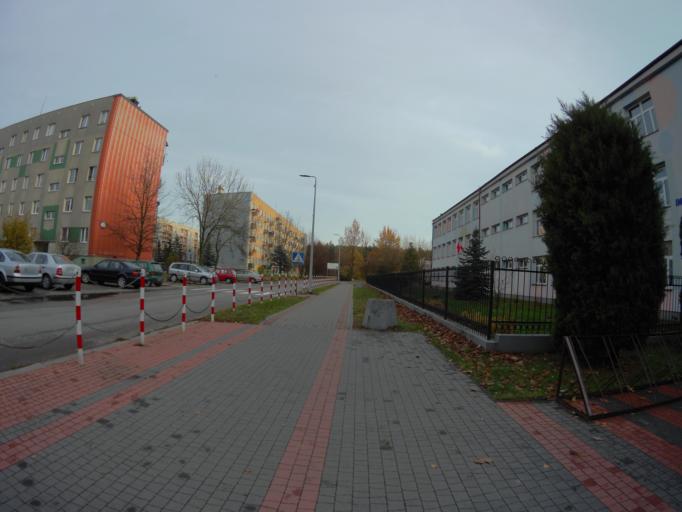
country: PL
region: Subcarpathian Voivodeship
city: Nowa Sarzyna
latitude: 50.3193
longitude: 22.3422
